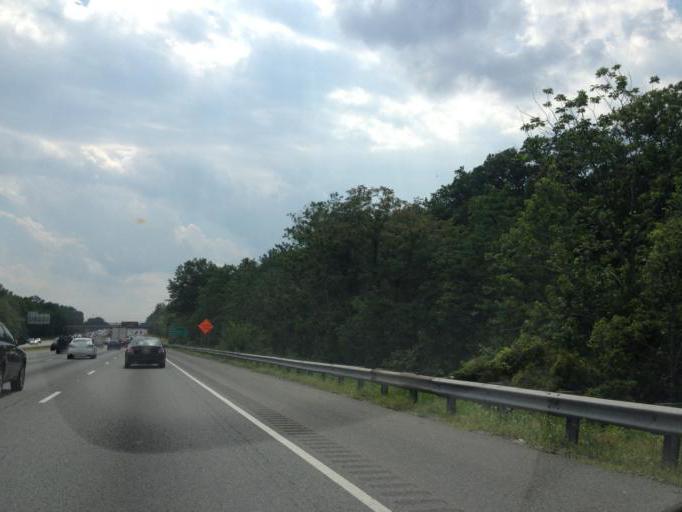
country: US
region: Maryland
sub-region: Howard County
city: West Elkridge
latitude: 39.2144
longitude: -76.7339
